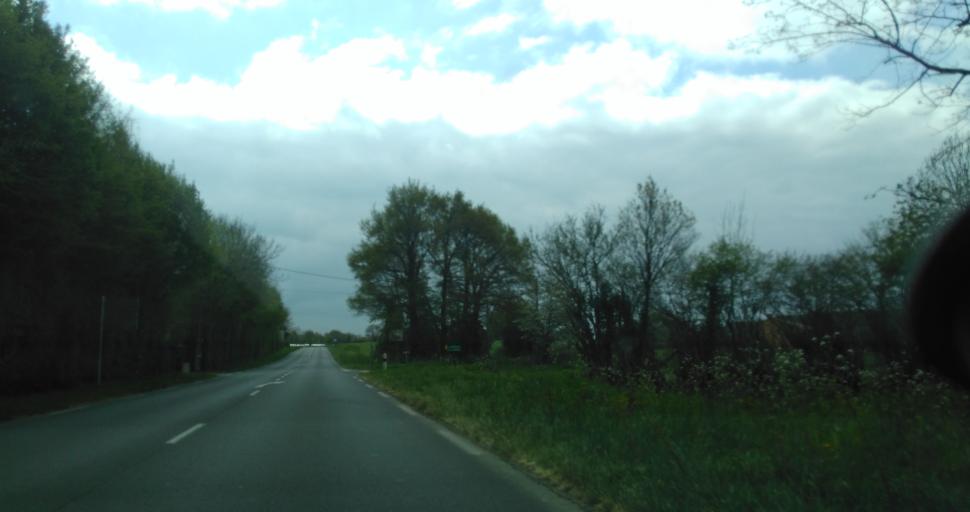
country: FR
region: Poitou-Charentes
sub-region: Departement des Deux-Sevres
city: La Foret-sur-Sevre
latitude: 46.7519
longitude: -0.6158
